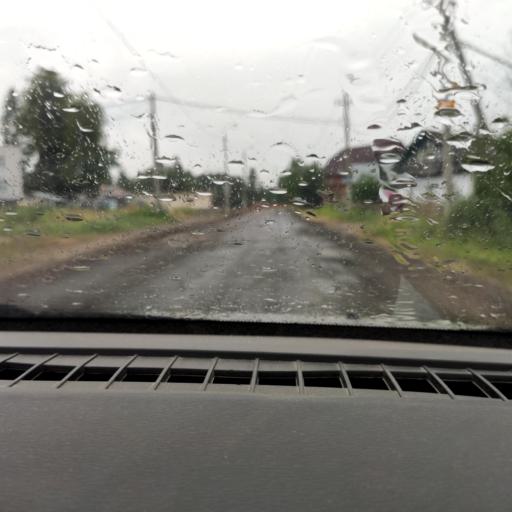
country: RU
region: Perm
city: Perm
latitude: 58.1034
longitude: 56.2891
